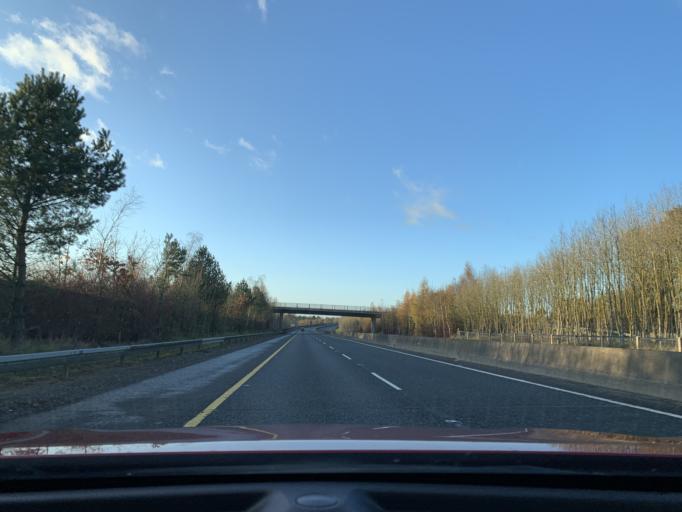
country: IE
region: Leinster
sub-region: An Iarmhi
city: Rathwire
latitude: 53.4861
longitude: -7.1883
